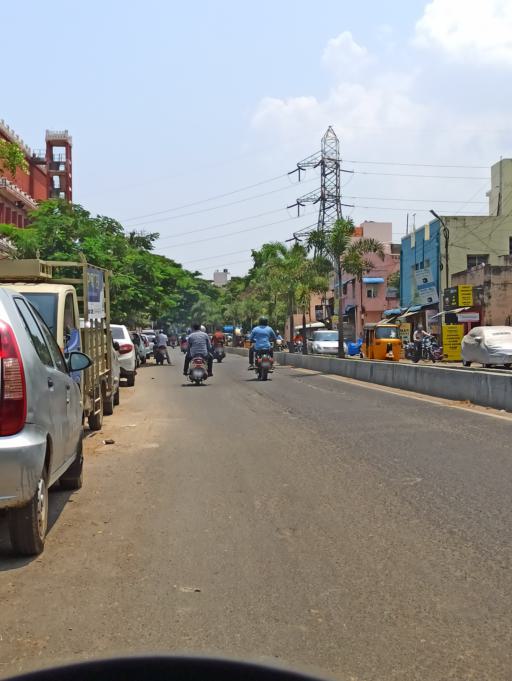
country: IN
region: Tamil Nadu
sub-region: Chennai
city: Chetput
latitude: 13.0901
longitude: 80.2316
